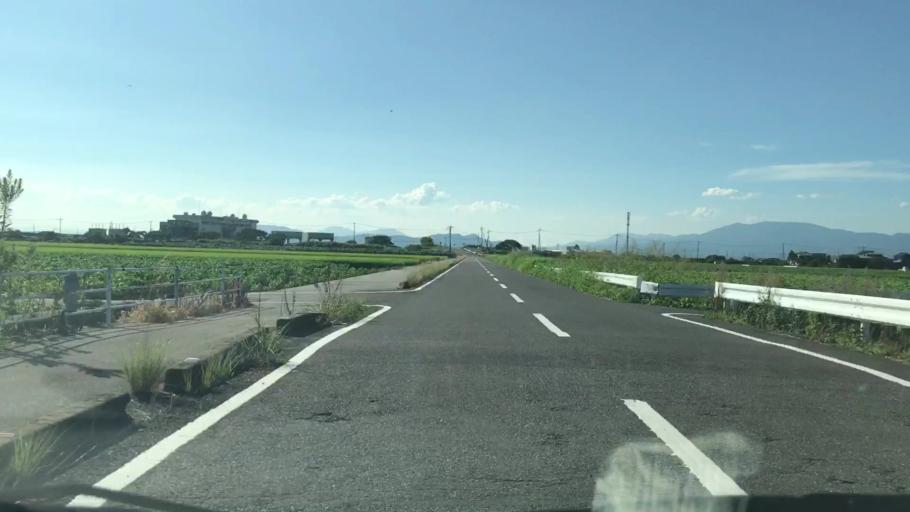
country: JP
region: Saga Prefecture
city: Okawa
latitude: 33.1840
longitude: 130.2956
